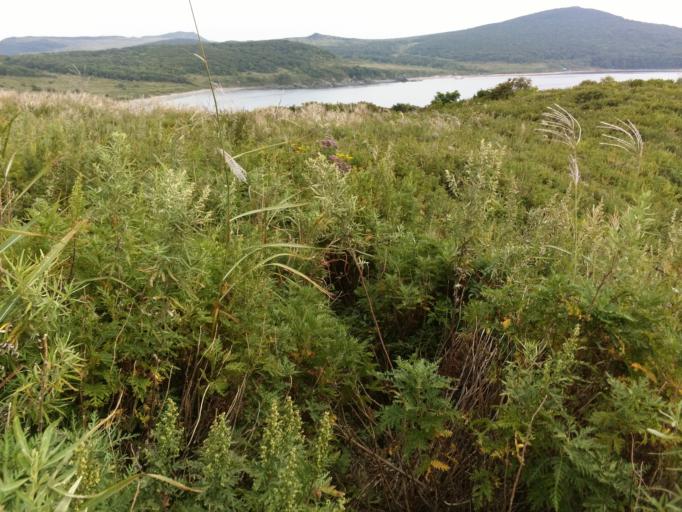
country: RU
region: Primorskiy
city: Popova
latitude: 42.9201
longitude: 131.7119
